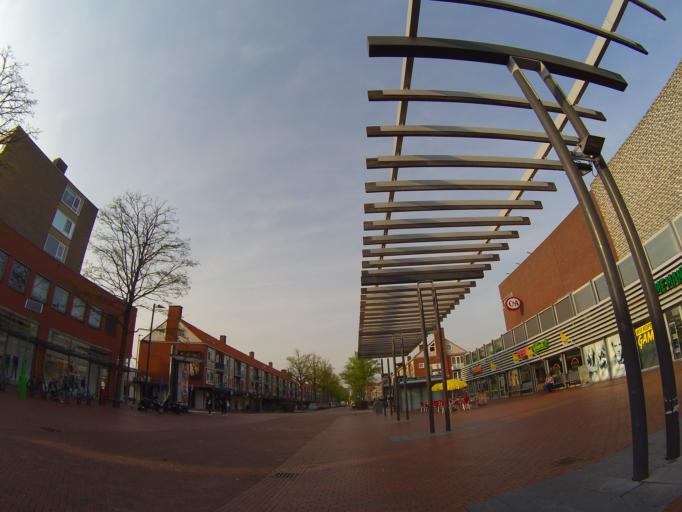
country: NL
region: North Holland
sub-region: Gemeente Amstelveen
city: Amstelveen
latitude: 52.3036
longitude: 4.8608
